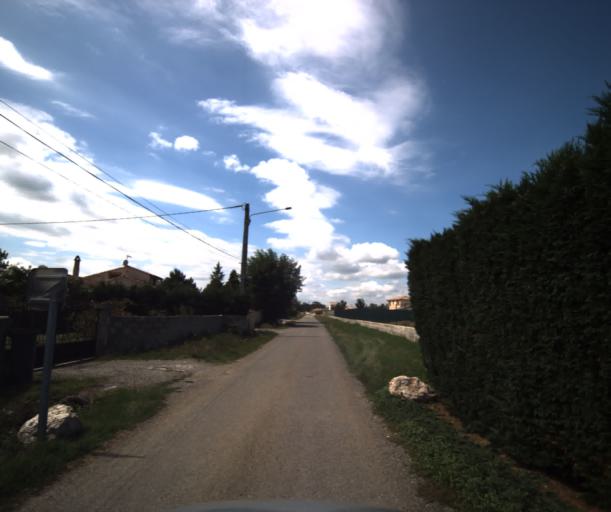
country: FR
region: Midi-Pyrenees
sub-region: Departement de la Haute-Garonne
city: Lacasse
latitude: 43.3888
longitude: 1.2613
